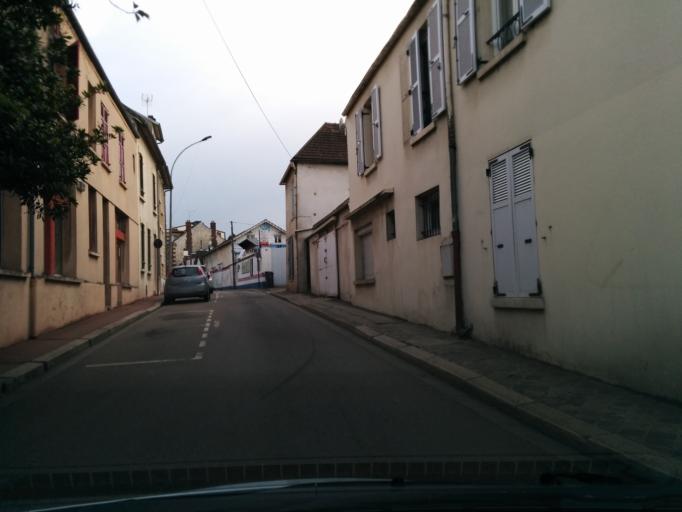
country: FR
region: Ile-de-France
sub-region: Departement des Yvelines
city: Mantes-la-Jolie
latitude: 48.9915
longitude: 1.7137
